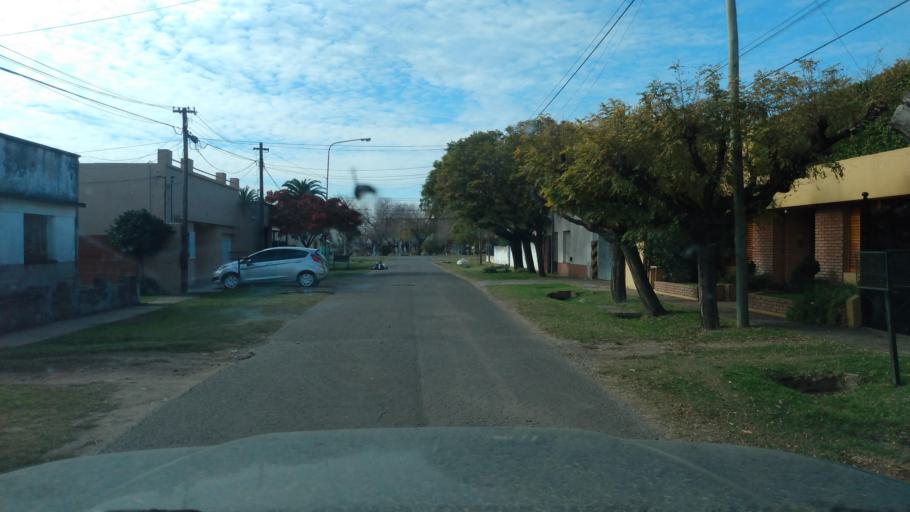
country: AR
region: Buenos Aires
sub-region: Partido de Lujan
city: Lujan
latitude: -34.5961
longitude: -59.1784
